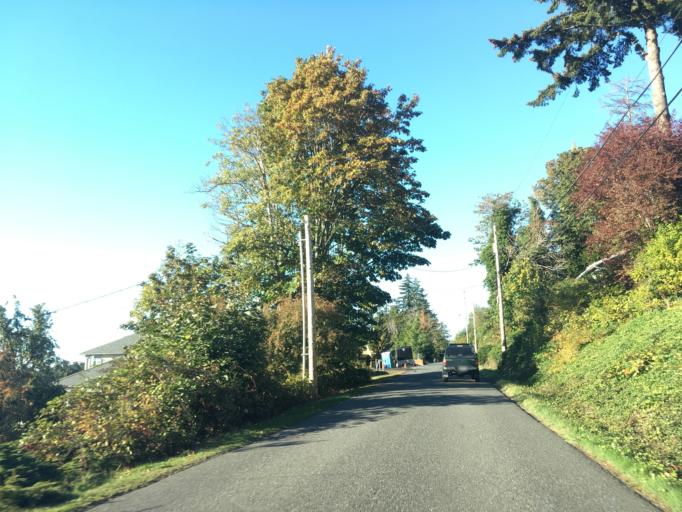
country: US
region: Washington
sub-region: Whatcom County
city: Bellingham
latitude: 48.7155
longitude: -122.4699
